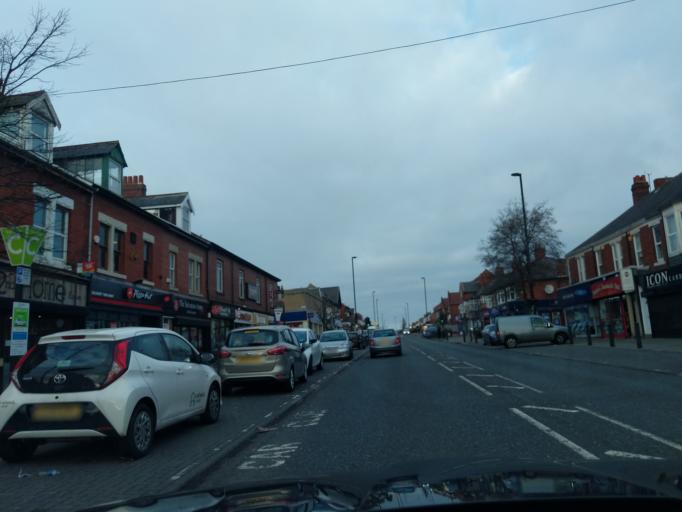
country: GB
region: England
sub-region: Gateshead
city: Felling
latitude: 54.9878
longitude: -1.5774
